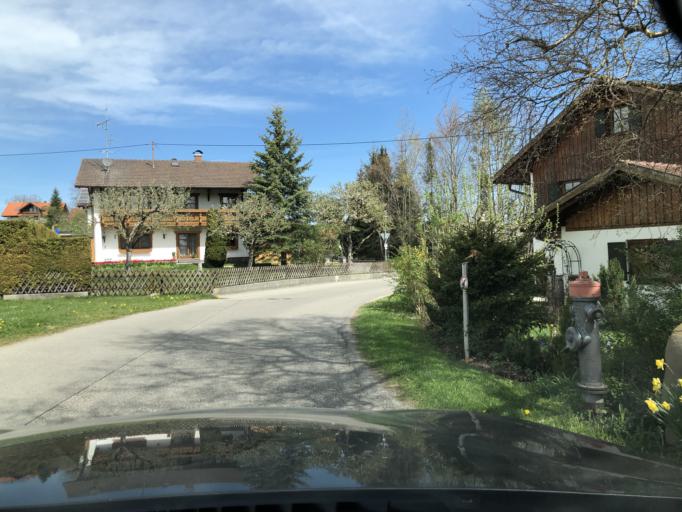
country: DE
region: Bavaria
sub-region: Swabia
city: Seeg
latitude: 47.6531
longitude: 10.6121
